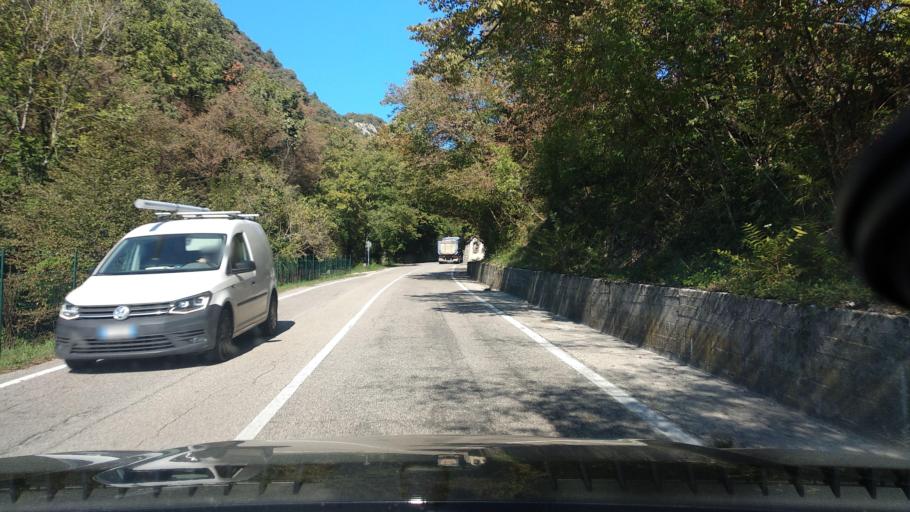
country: IT
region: Veneto
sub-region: Provincia di Verona
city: Garda
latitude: 45.5861
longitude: 10.7003
